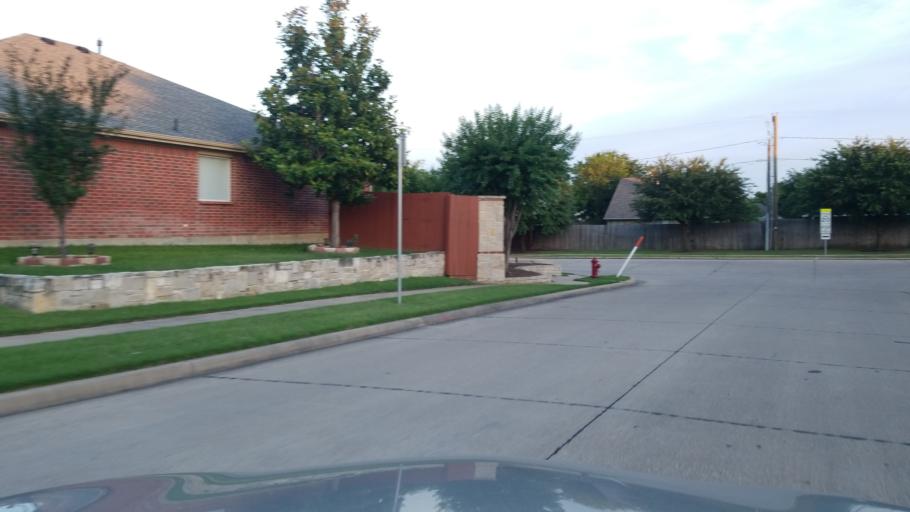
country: US
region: Texas
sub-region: Dallas County
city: Grand Prairie
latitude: 32.6845
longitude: -97.0408
